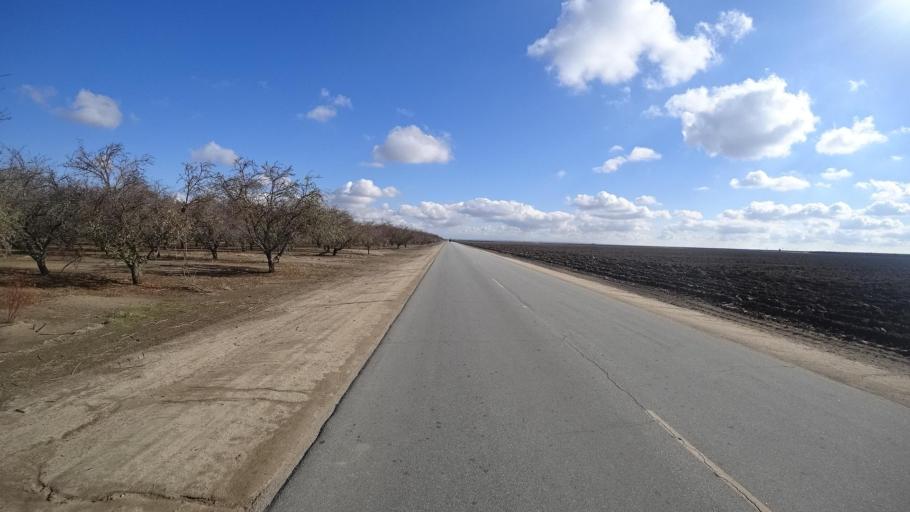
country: US
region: California
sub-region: Kern County
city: McFarland
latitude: 35.6743
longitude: -119.2928
